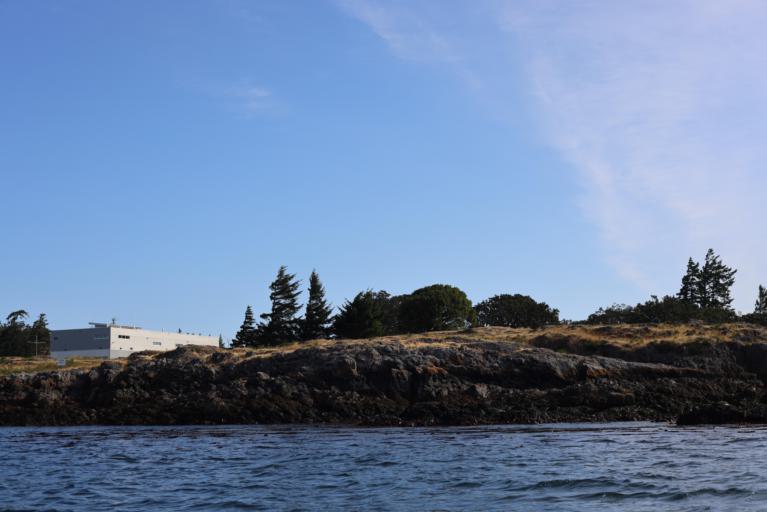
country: CA
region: British Columbia
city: Metchosin
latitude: 48.3366
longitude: -123.5419
